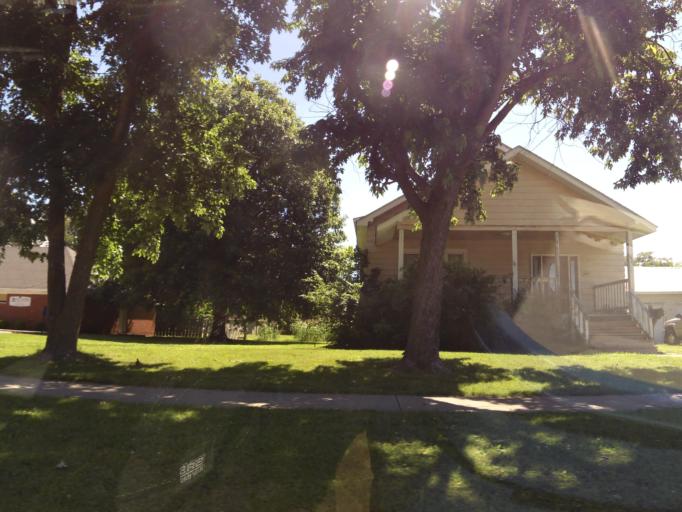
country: US
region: Missouri
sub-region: New Madrid County
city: New Madrid
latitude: 36.5907
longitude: -89.5272
